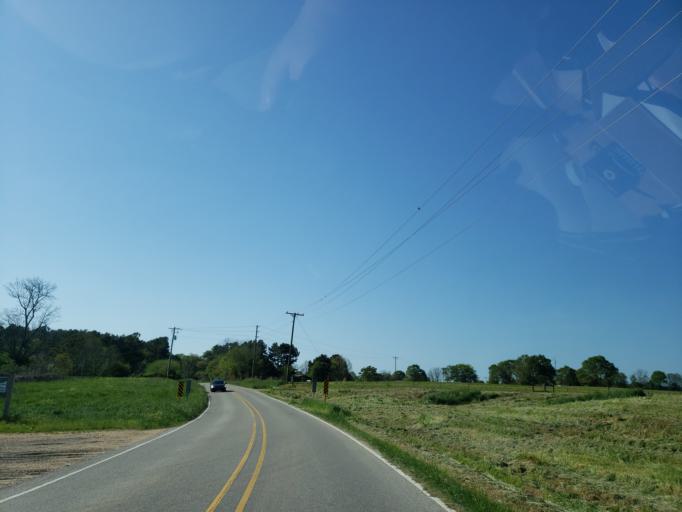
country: US
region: Mississippi
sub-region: Jones County
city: Ellisville
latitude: 31.5580
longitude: -89.3662
